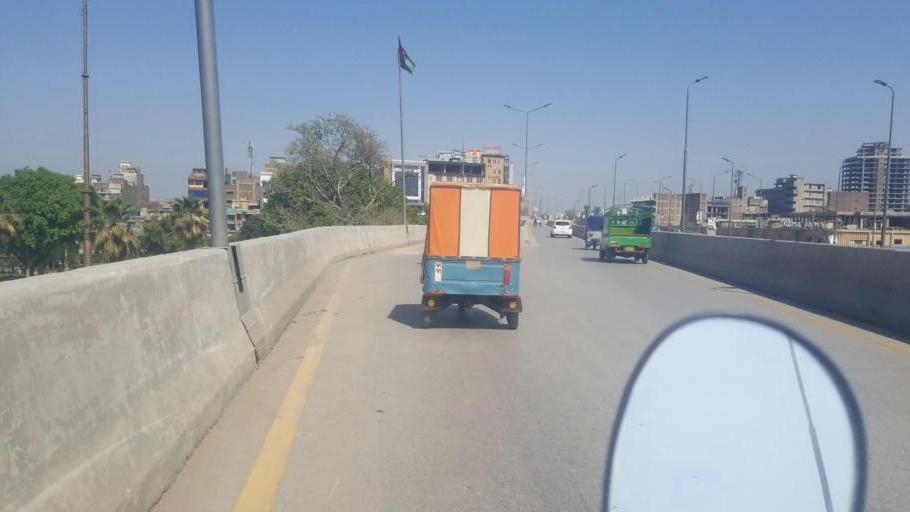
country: PK
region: Khyber Pakhtunkhwa
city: Peshawar
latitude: 34.0148
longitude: 71.5699
